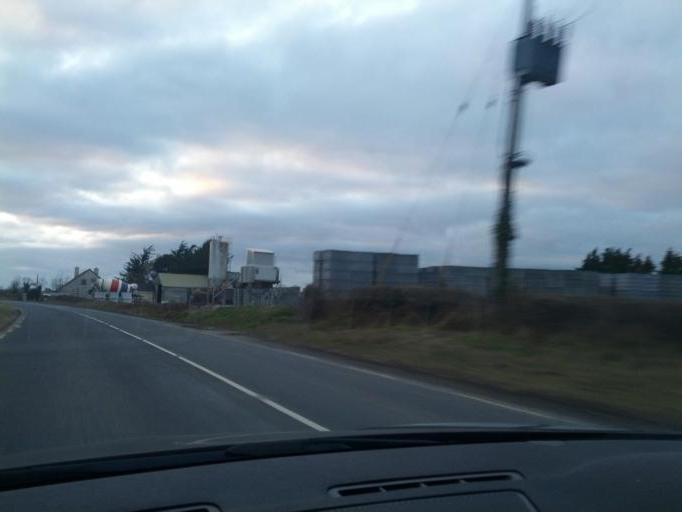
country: IE
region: Leinster
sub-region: Uibh Fhaili
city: Banagher
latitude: 53.1029
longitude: -8.0129
